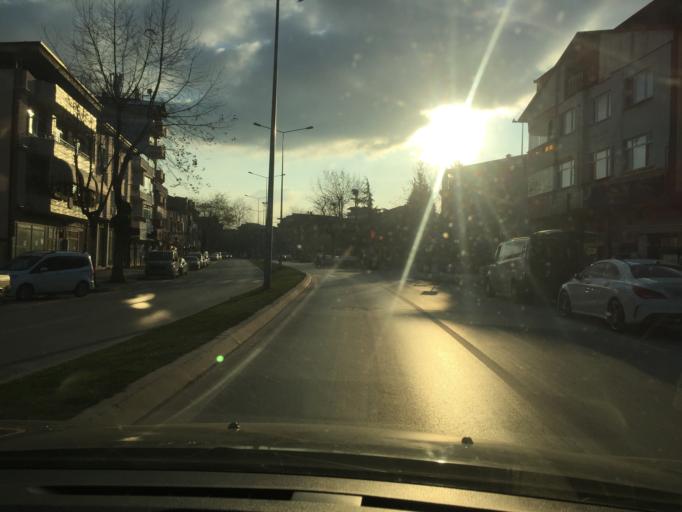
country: TR
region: Sakarya
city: Adapazari
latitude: 40.7862
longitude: 30.4007
